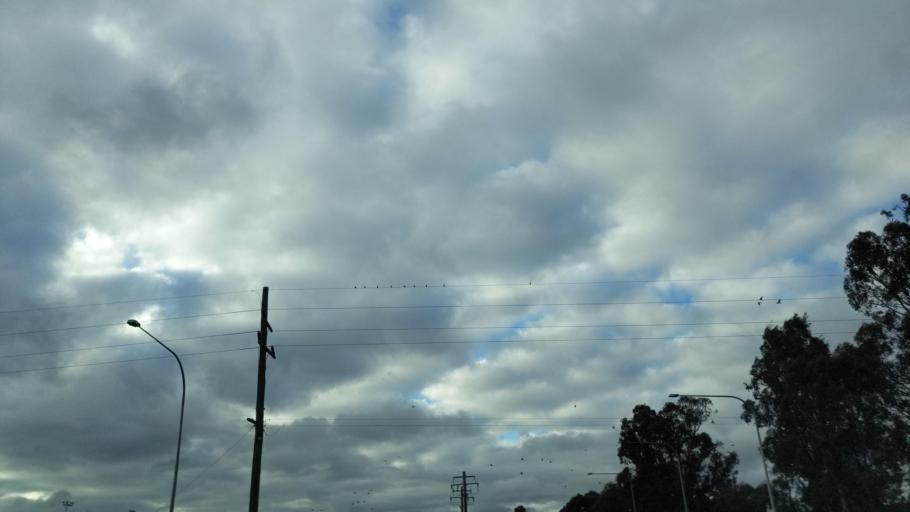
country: AU
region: New South Wales
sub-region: Wagga Wagga
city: Wagga Wagga
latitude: -35.0773
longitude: 147.3865
